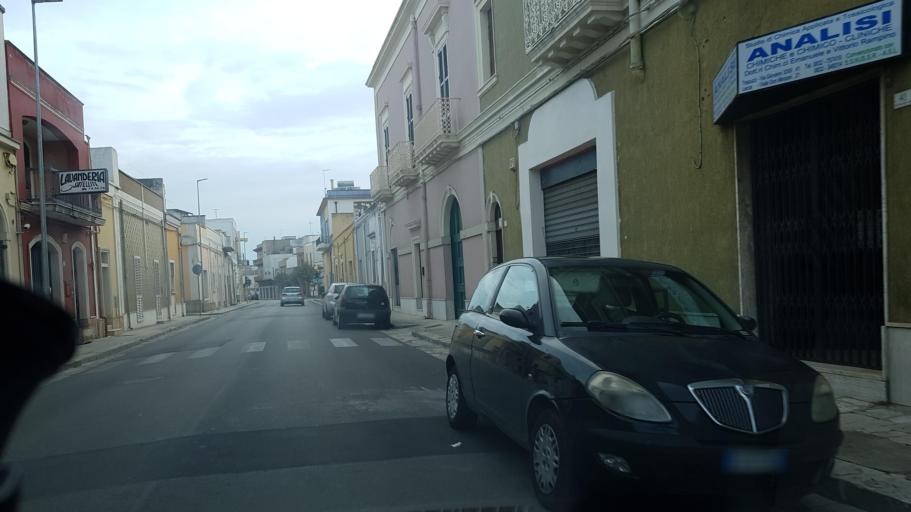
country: IT
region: Apulia
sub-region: Provincia di Lecce
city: Trepuzzi
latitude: 40.4073
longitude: 18.0692
